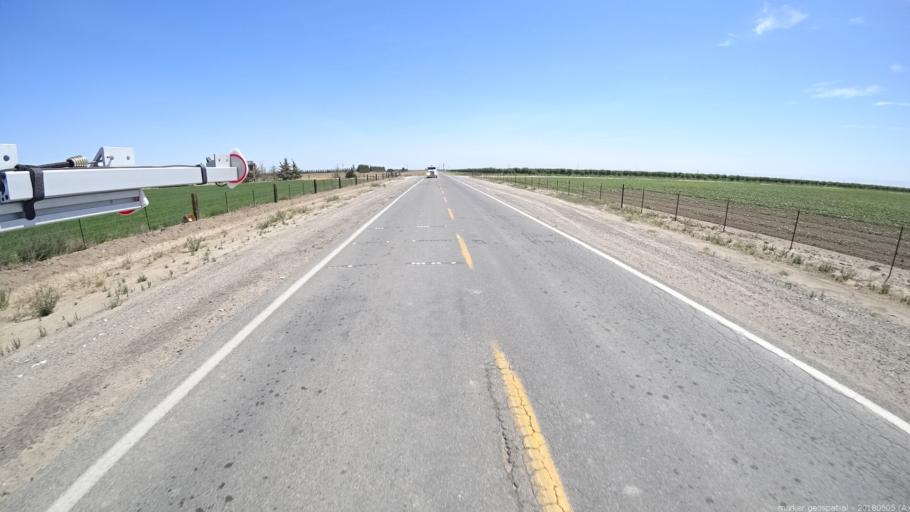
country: US
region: California
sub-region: Madera County
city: Chowchilla
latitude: 37.0156
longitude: -120.3834
